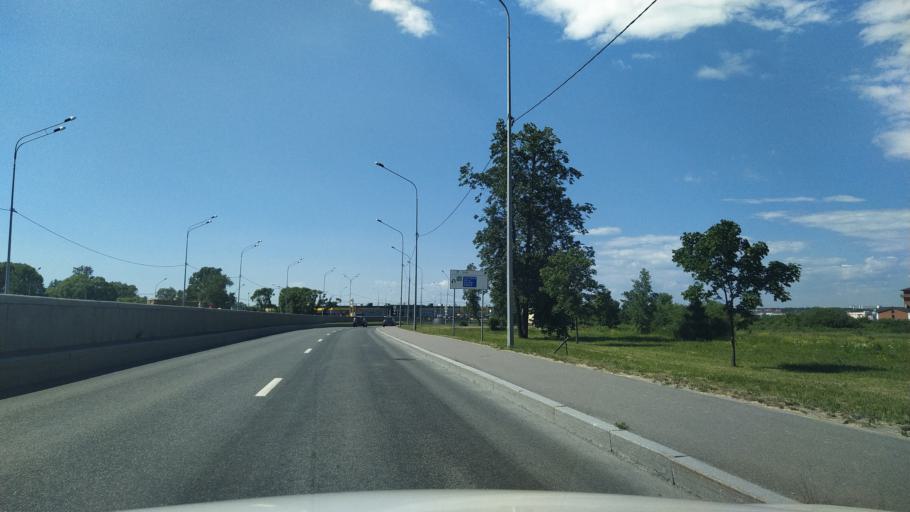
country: RU
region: St.-Petersburg
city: Aleksandrovskaya
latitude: 59.7762
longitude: 30.3289
